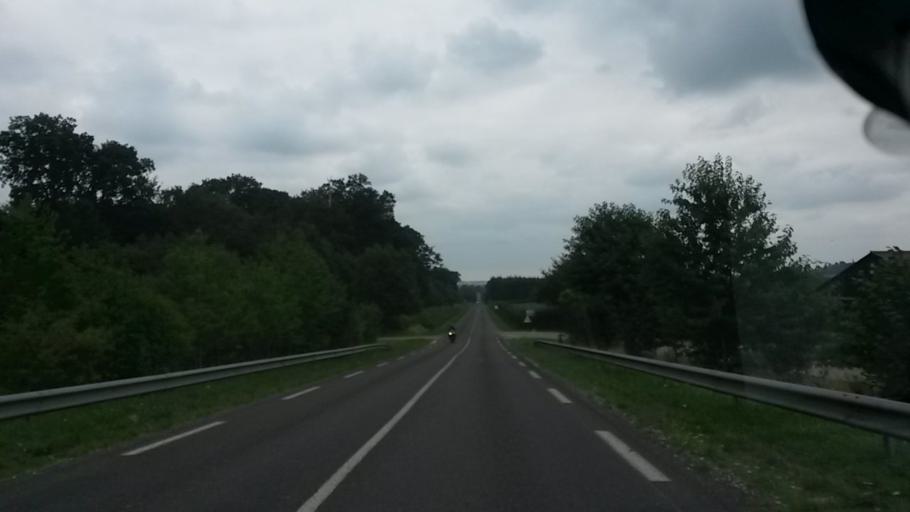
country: FR
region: Haute-Normandie
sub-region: Departement de la Seine-Maritime
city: Forges-les-Eaux
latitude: 49.6009
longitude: 1.5467
